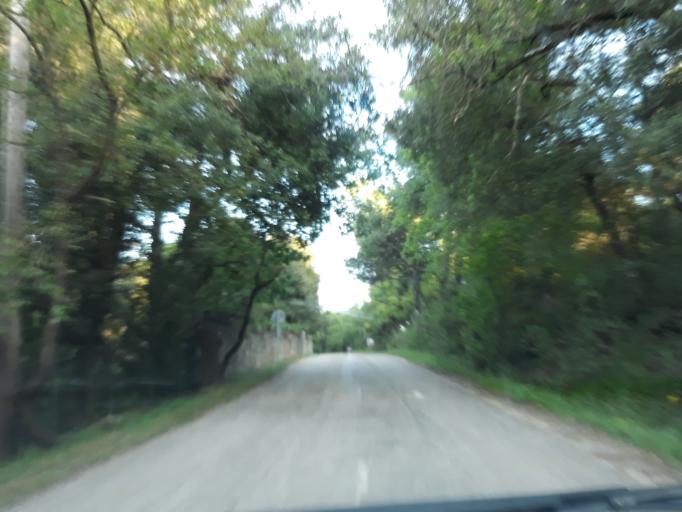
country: GR
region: Attica
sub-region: Nomarchia Anatolikis Attikis
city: Afidnes
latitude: 38.2159
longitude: 23.7863
